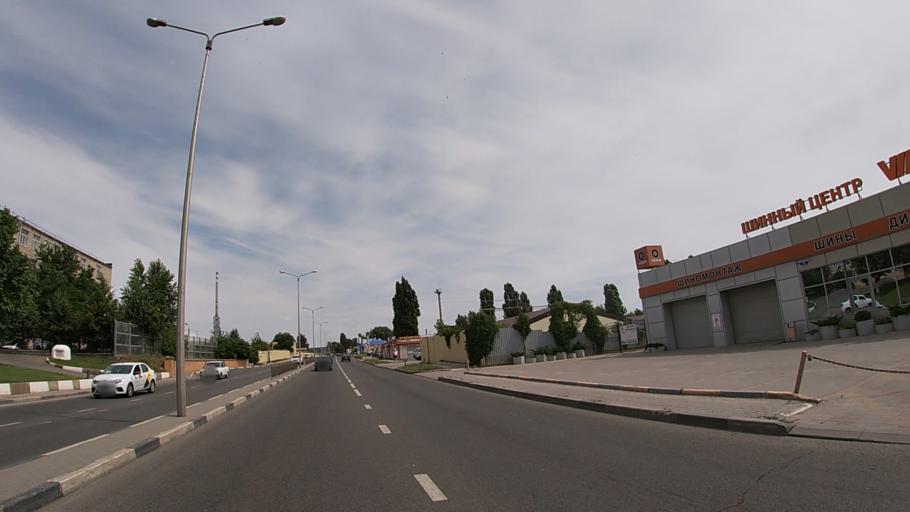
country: RU
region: Belgorod
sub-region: Belgorodskiy Rayon
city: Belgorod
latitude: 50.6143
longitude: 36.5365
